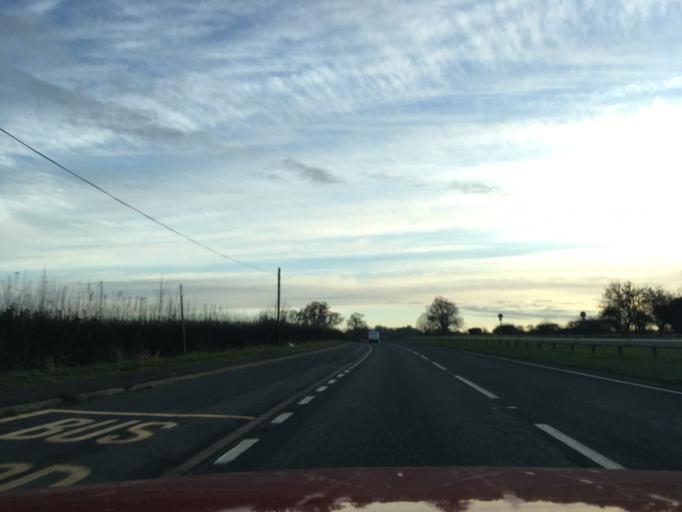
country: GB
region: England
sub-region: Staffordshire
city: Stone
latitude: 52.8714
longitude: -2.1302
